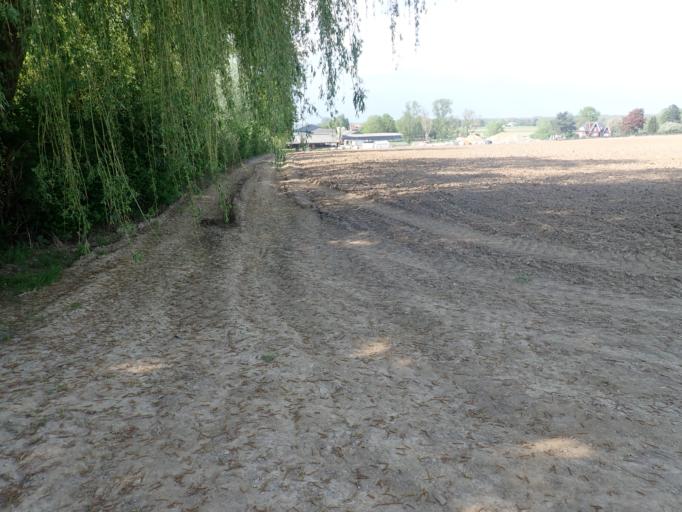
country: BE
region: Flanders
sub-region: Provincie Vlaams-Brabant
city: Wemmel
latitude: 50.9355
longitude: 4.2893
